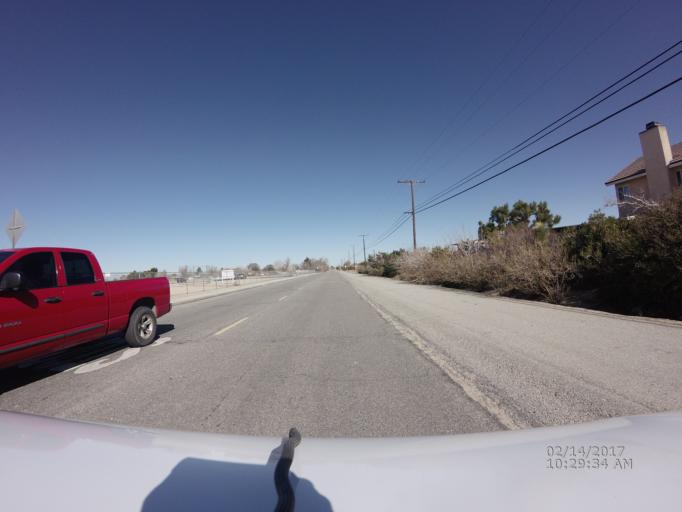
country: US
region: California
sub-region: Los Angeles County
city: Littlerock
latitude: 34.5599
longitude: -117.9520
